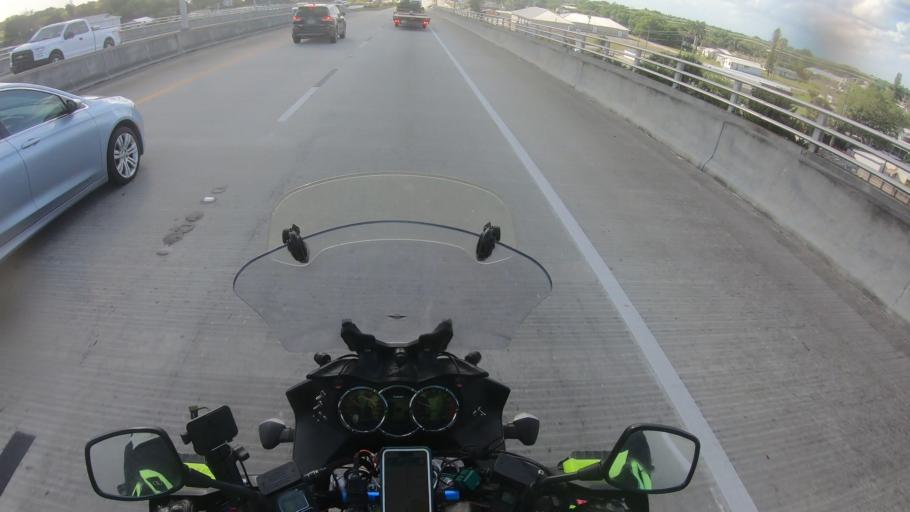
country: US
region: Florida
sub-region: Glades County
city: Moore Haven
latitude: 26.8335
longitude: -81.0916
